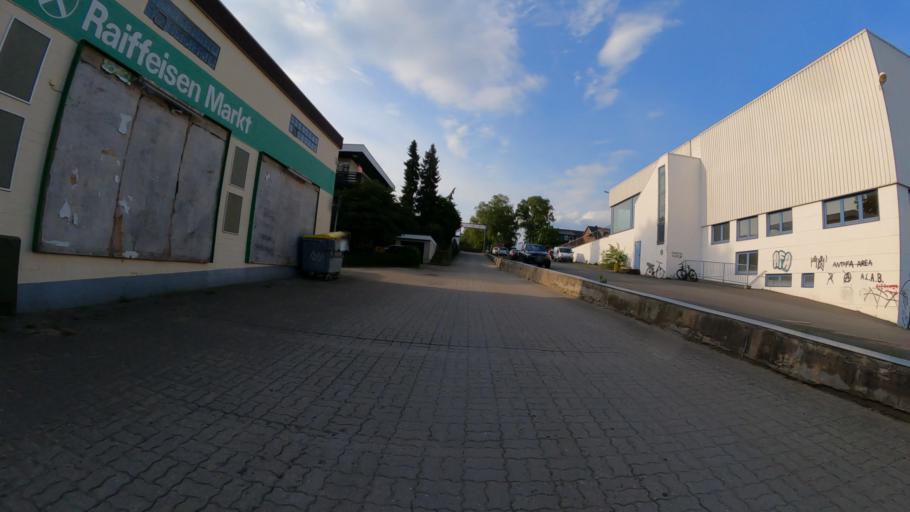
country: DE
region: Lower Saxony
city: Buchholz in der Nordheide
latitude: 53.3247
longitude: 9.8703
